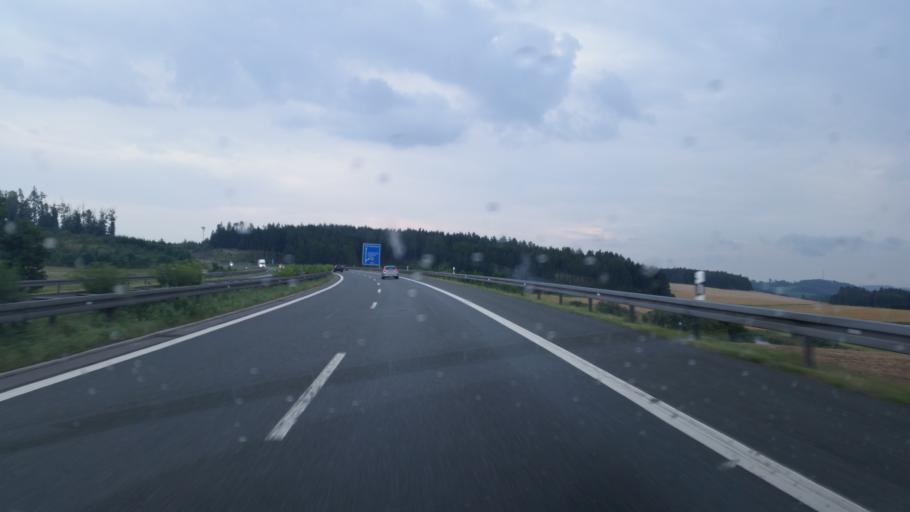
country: DE
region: Bavaria
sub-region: Upper Franconia
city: Trogen
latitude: 50.3595
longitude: 11.9698
